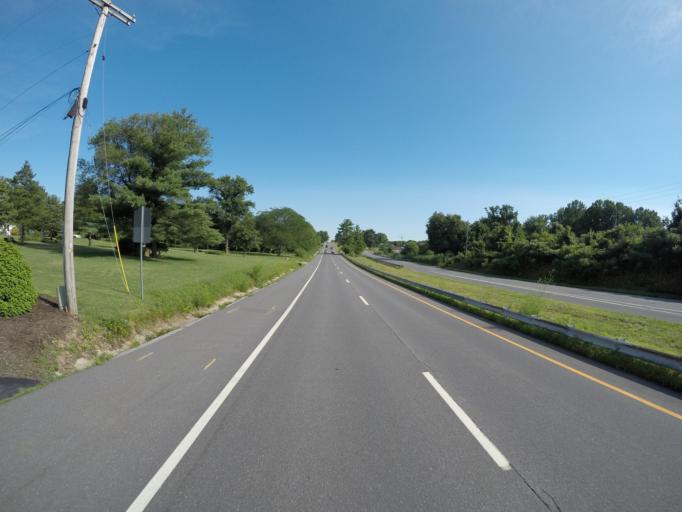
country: US
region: Delaware
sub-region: New Castle County
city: Bear
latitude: 39.5680
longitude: -75.6547
